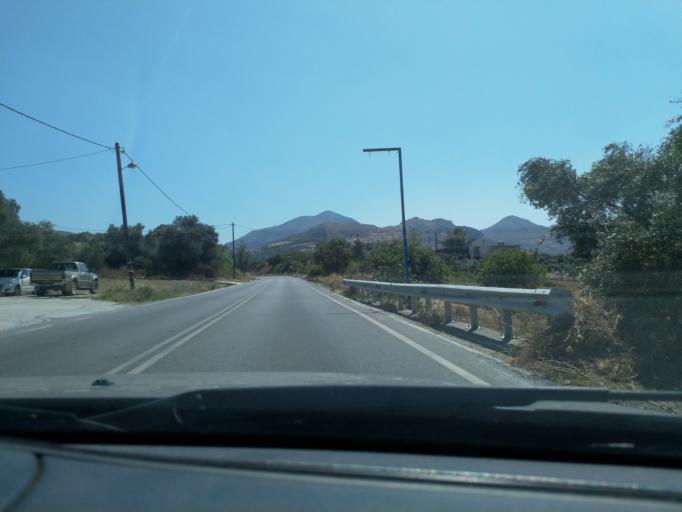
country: GR
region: Crete
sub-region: Nomos Rethymnis
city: Atsipopoulon
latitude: 35.2294
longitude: 24.4749
